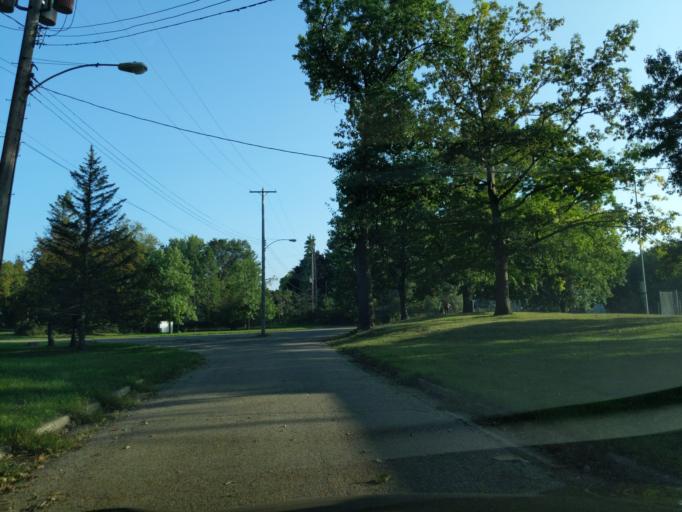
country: US
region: Michigan
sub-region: Ingham County
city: Lansing
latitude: 42.7166
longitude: -84.5360
